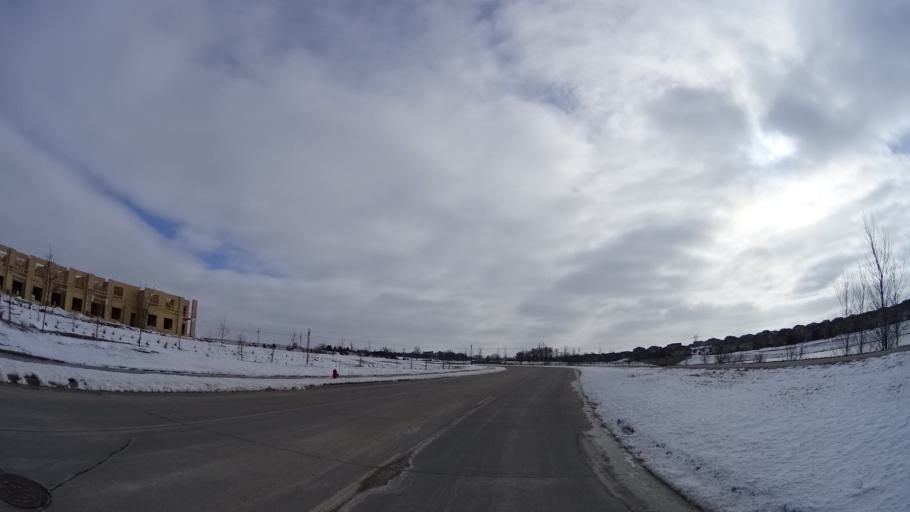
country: US
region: Nebraska
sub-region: Sarpy County
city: Papillion
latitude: 41.1301
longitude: -96.0259
